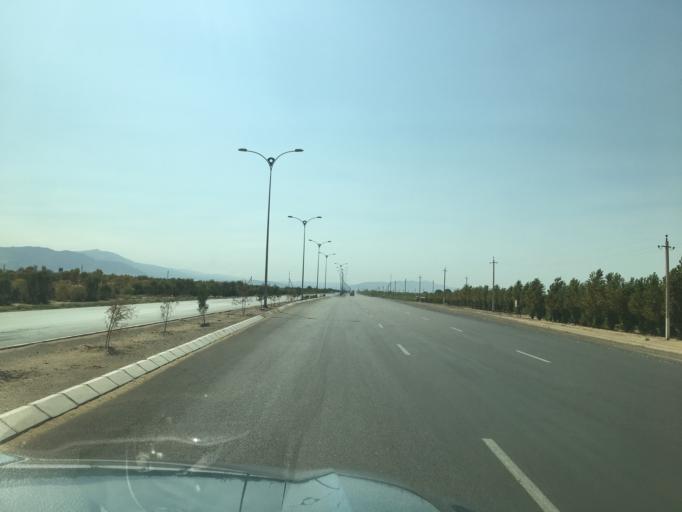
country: TM
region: Ahal
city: Abadan
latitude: 38.1028
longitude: 58.3079
